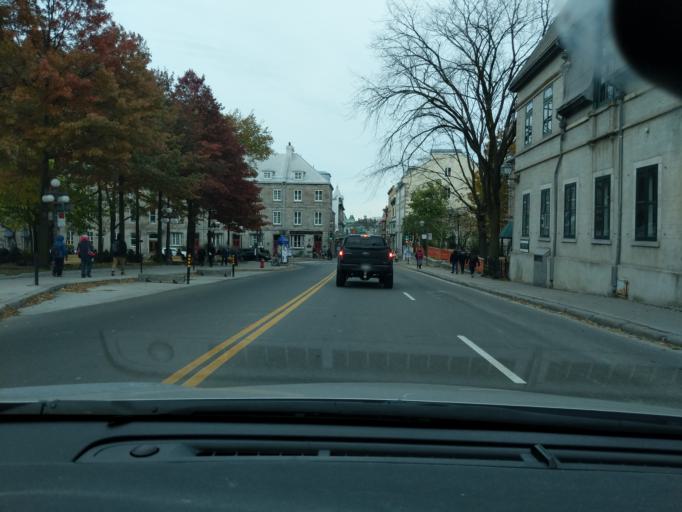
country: CA
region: Quebec
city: Quebec
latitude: 46.8097
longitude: -71.2109
